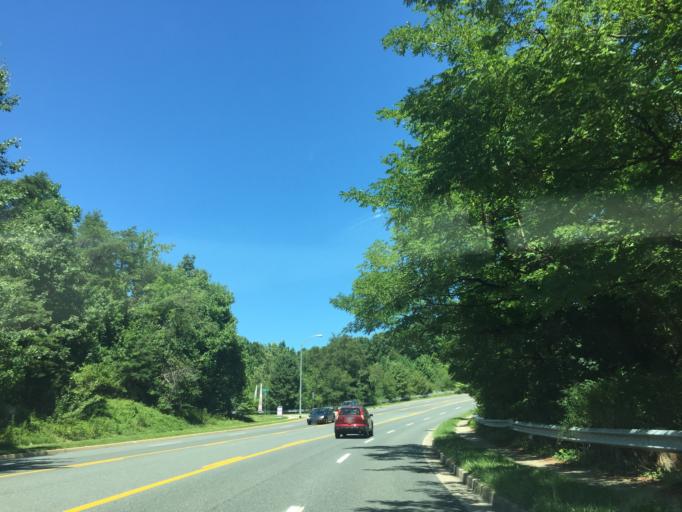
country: US
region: Maryland
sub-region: Baltimore County
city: Carney
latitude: 39.3865
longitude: -76.5092
